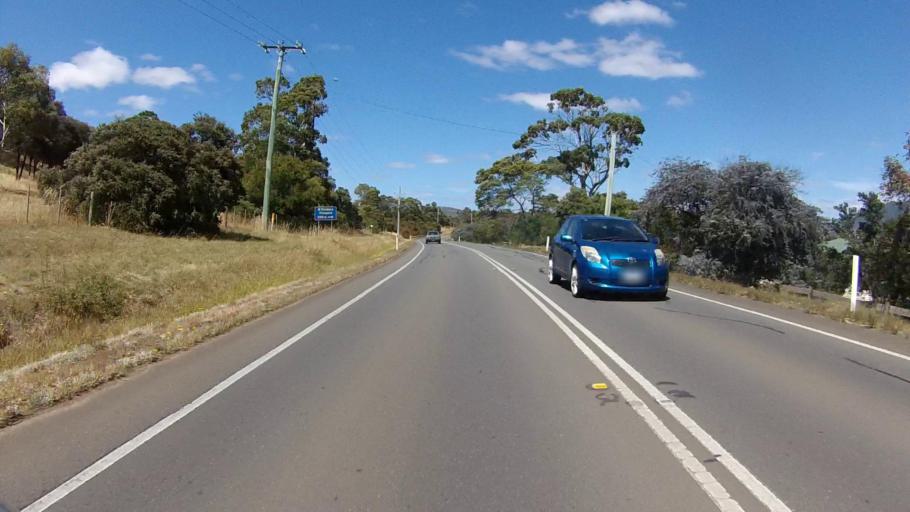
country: AU
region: Tasmania
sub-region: Clarence
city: Cambridge
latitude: -42.7443
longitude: 147.4192
